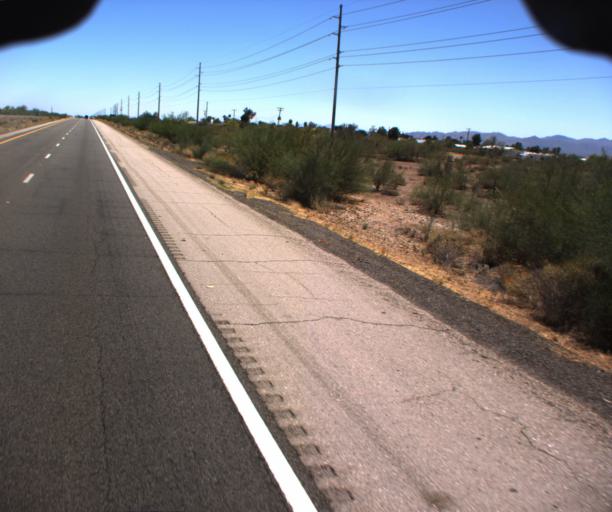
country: US
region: Arizona
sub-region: Maricopa County
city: Wickenburg
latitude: 33.8209
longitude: -112.5841
